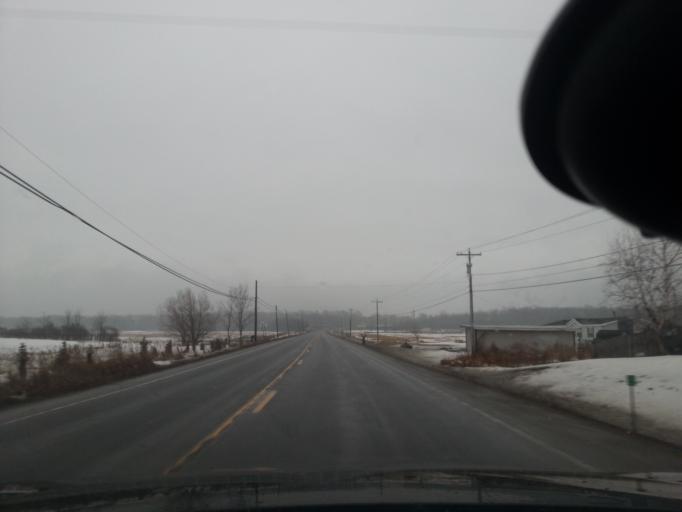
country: US
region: New York
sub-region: St. Lawrence County
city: Ogdensburg
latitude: 44.6625
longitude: -75.4623
